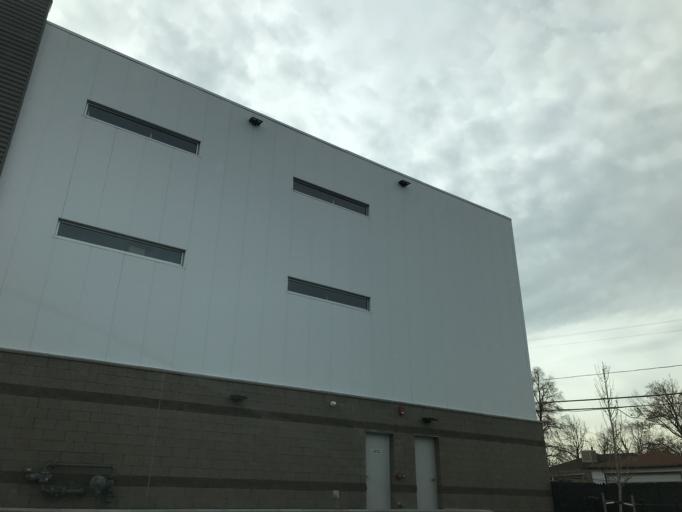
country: US
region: Colorado
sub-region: Adams County
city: Commerce City
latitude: 39.7676
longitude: -104.9050
